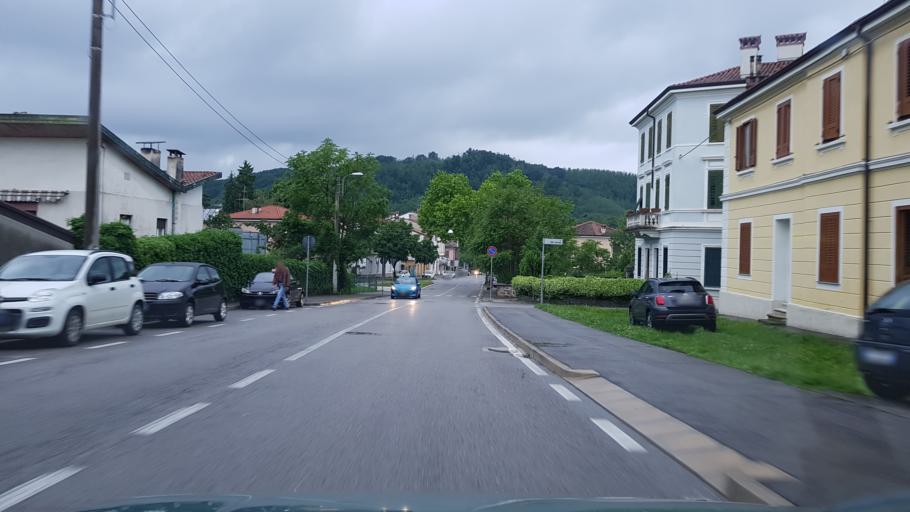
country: IT
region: Friuli Venezia Giulia
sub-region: Provincia di Gorizia
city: Gorizia
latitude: 45.9542
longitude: 13.6168
